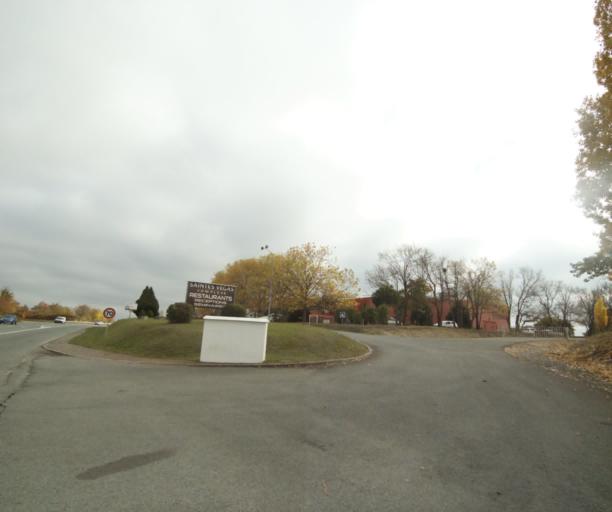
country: FR
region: Poitou-Charentes
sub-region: Departement de la Charente-Maritime
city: Saintes
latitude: 45.7457
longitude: -0.6730
